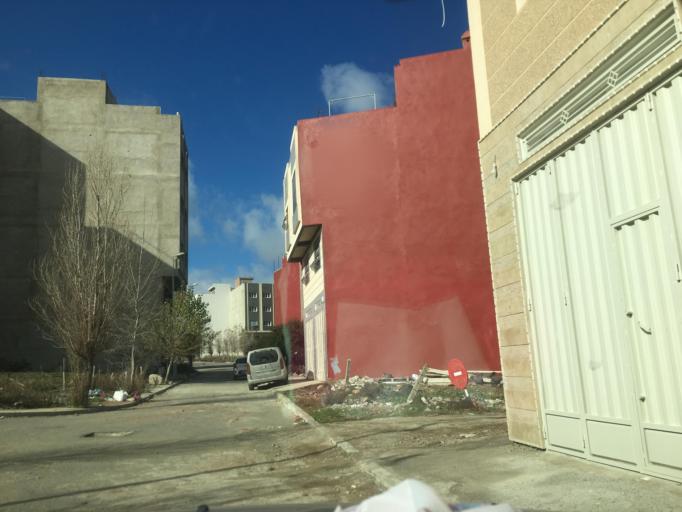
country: MA
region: Tanger-Tetouan
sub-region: Tanger-Assilah
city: Tangier
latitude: 35.7084
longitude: -5.8152
